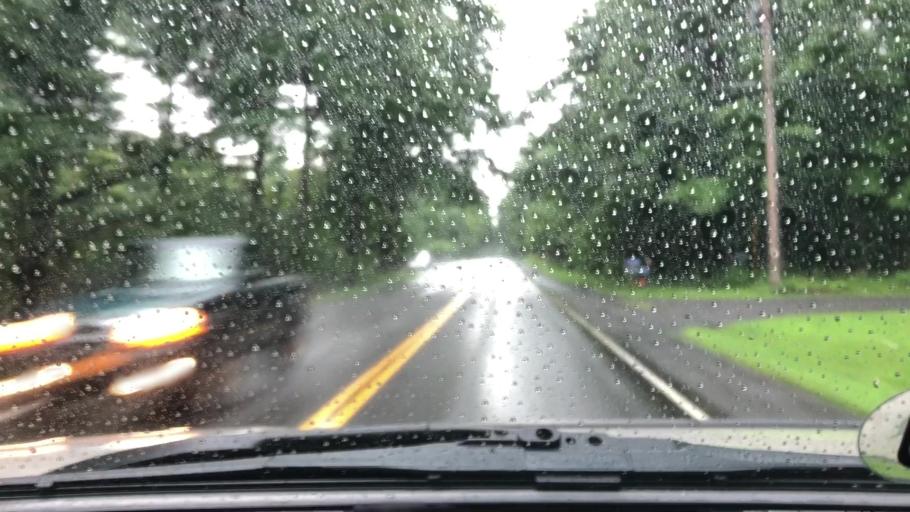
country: US
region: New York
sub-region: Greene County
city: Palenville
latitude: 42.1714
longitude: -73.9887
